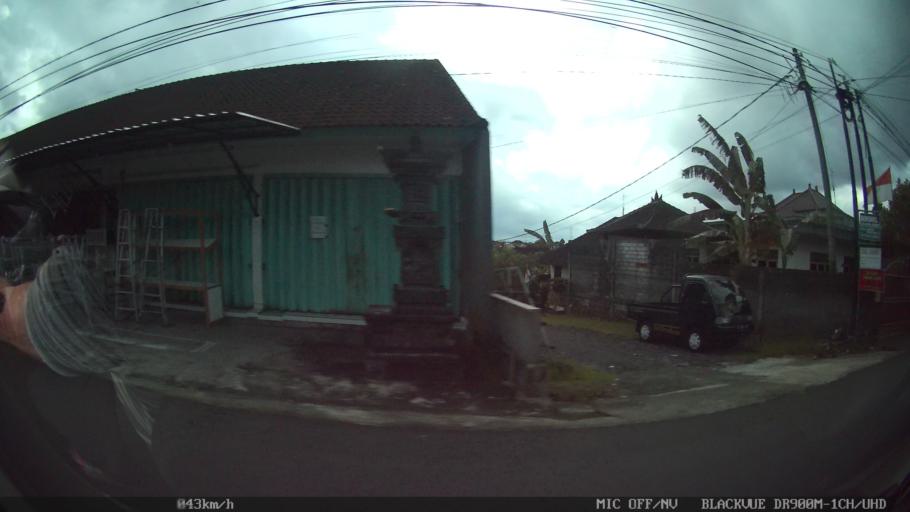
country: ID
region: Bali
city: Banjar Tegal Belodan
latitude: -8.5429
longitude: 115.1165
